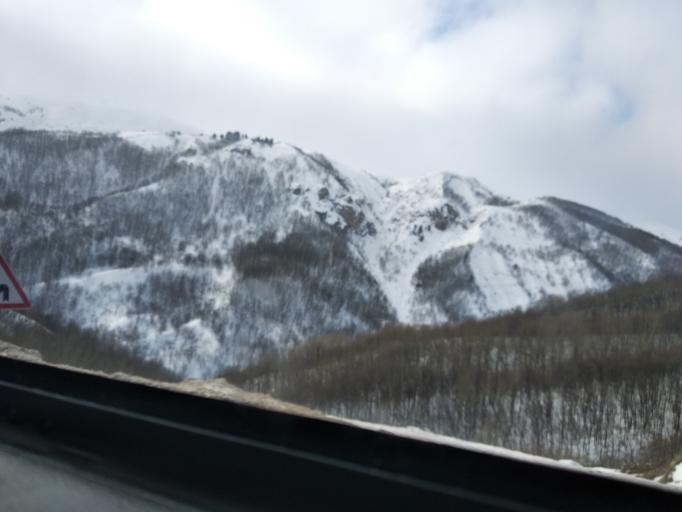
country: TR
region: Erzincan
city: Catalarmut
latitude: 39.8966
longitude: 39.3863
